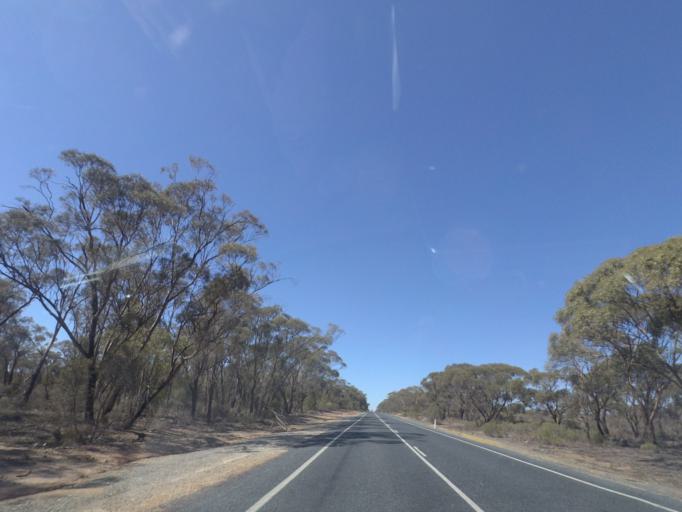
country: AU
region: New South Wales
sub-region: Bland
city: West Wyalong
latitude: -34.1229
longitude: 147.1266
